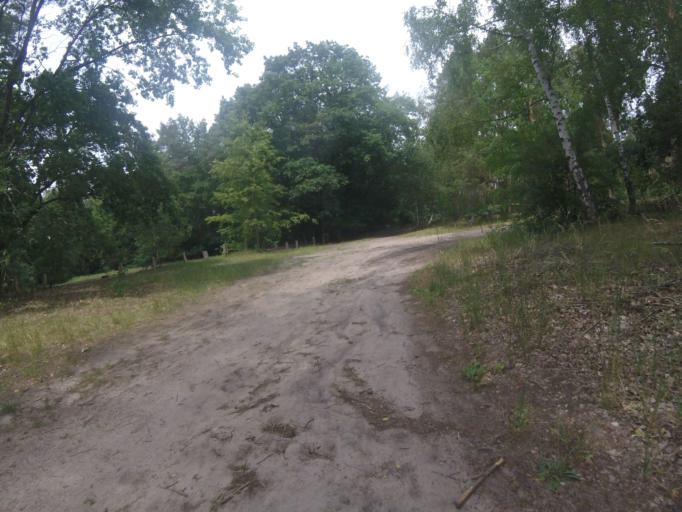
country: DE
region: Brandenburg
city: Konigs Wusterhausen
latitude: 52.2679
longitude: 13.6091
